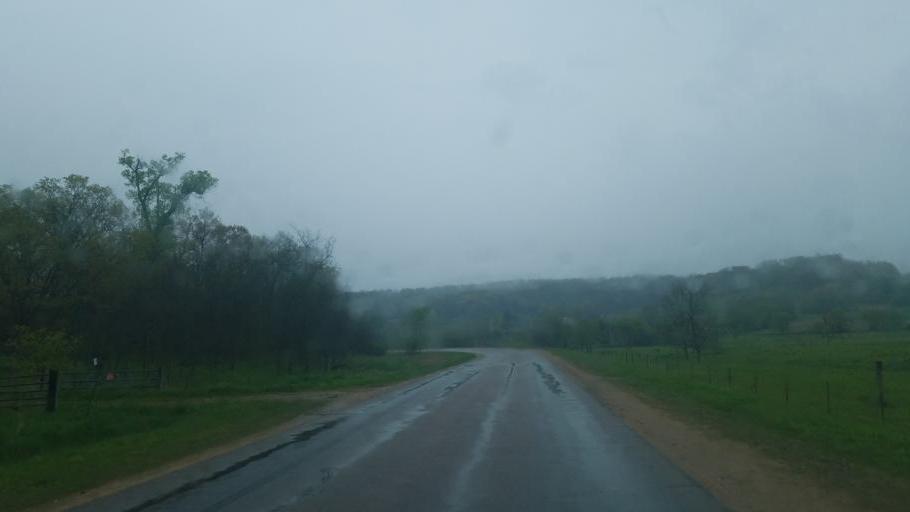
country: US
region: Wisconsin
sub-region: Vernon County
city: Hillsboro
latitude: 43.6118
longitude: -90.3611
